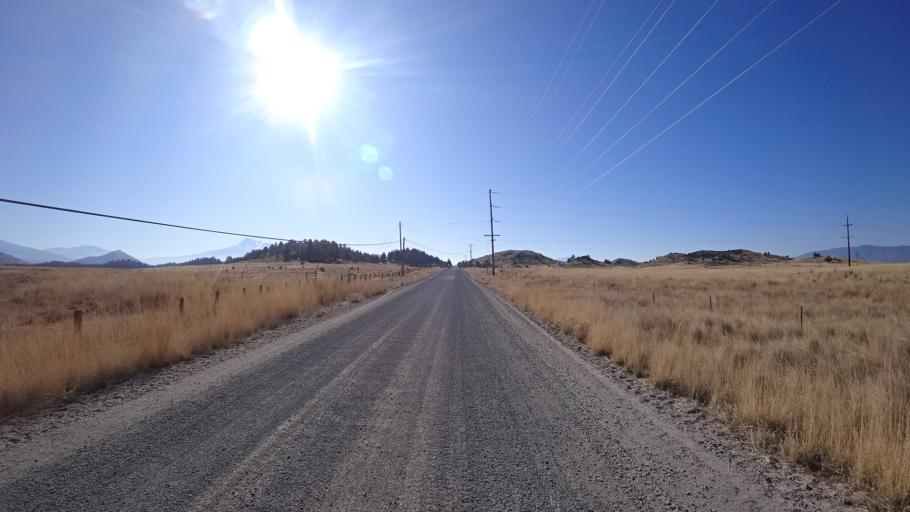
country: US
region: California
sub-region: Siskiyou County
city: Montague
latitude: 41.7048
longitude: -122.4377
